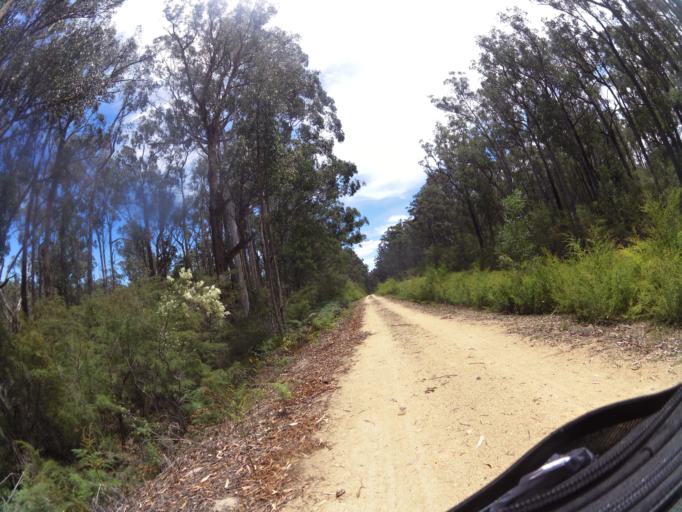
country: AU
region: Victoria
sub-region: East Gippsland
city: Lakes Entrance
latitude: -37.7409
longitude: 148.0259
